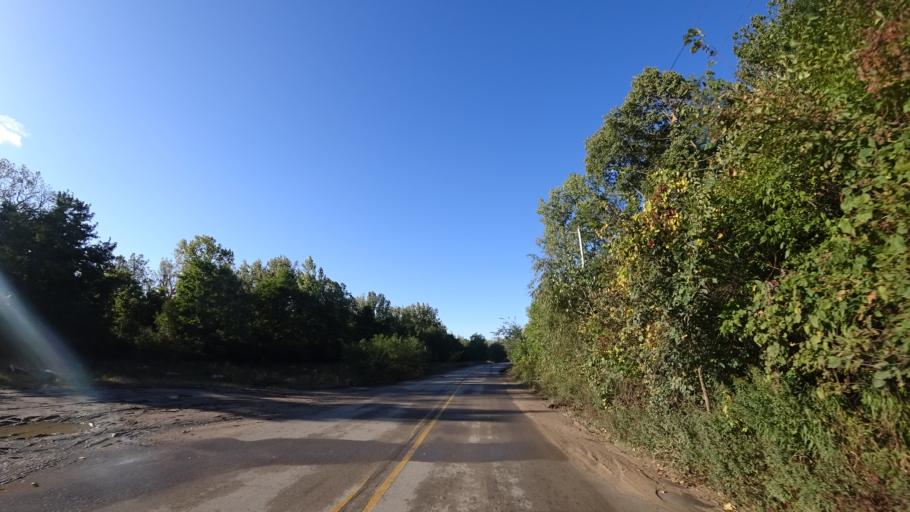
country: US
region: Michigan
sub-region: Kent County
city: Wyoming
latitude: 42.9501
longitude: -85.7115
